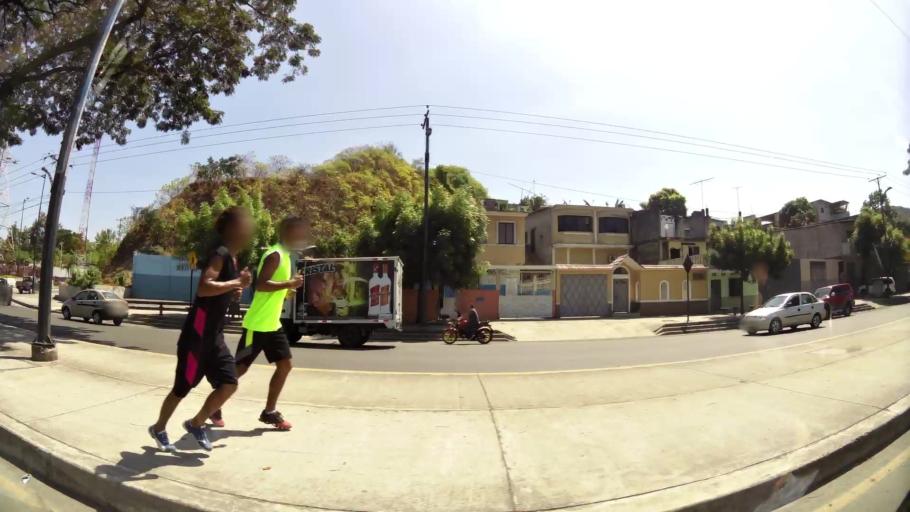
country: EC
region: Guayas
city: Guayaquil
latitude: -2.1898
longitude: -79.9315
